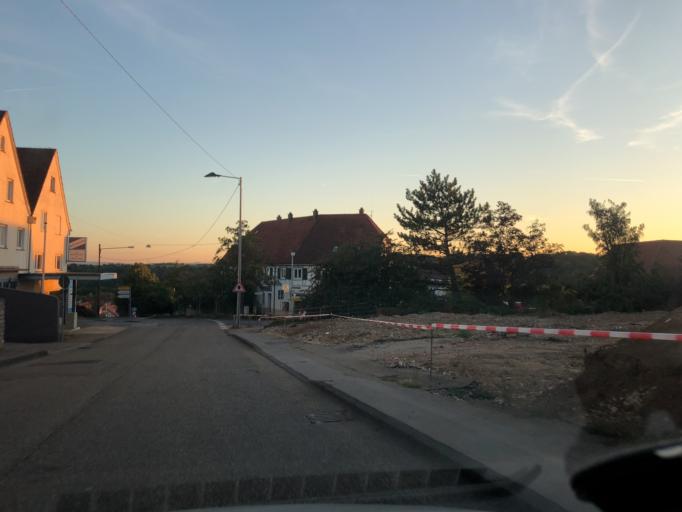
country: DE
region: Baden-Wuerttemberg
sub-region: Regierungsbezirk Stuttgart
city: Marbach am Neckar
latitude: 48.9068
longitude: 9.2656
